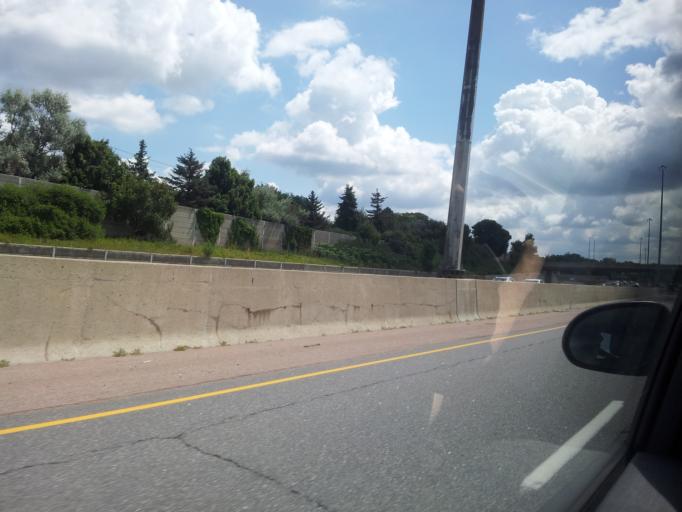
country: CA
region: Ontario
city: Kitchener
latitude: 43.4482
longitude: -80.4627
